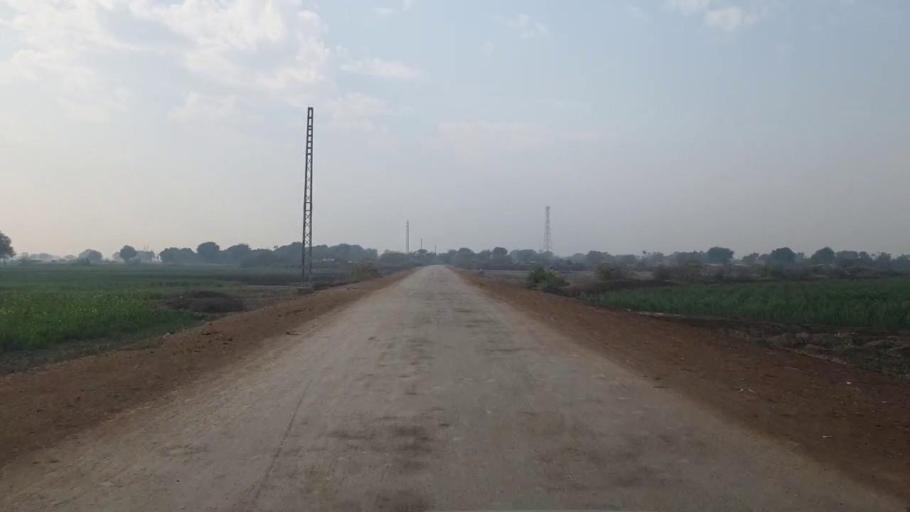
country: PK
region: Sindh
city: Hala
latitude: 25.8975
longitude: 68.4091
